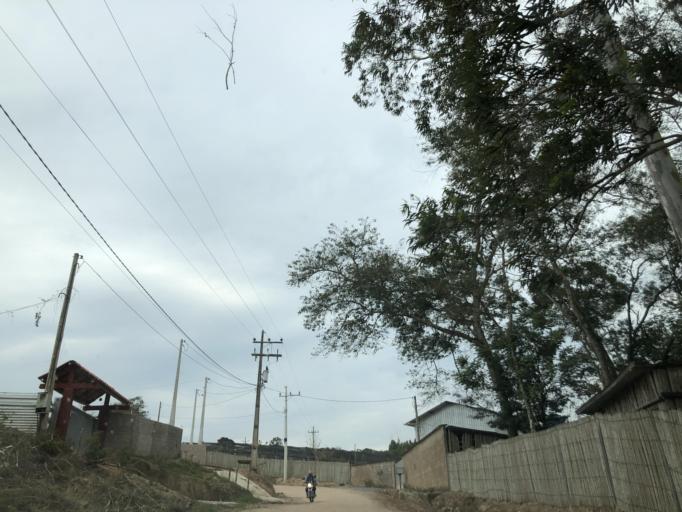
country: BR
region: Sao Paulo
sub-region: Pilar Do Sul
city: Pilar do Sul
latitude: -23.8181
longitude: -47.6310
